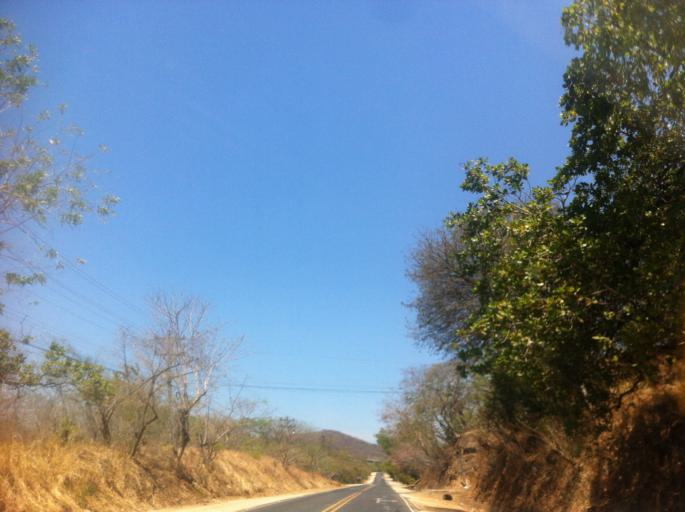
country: CR
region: Guanacaste
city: Belen
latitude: 10.3552
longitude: -85.5684
